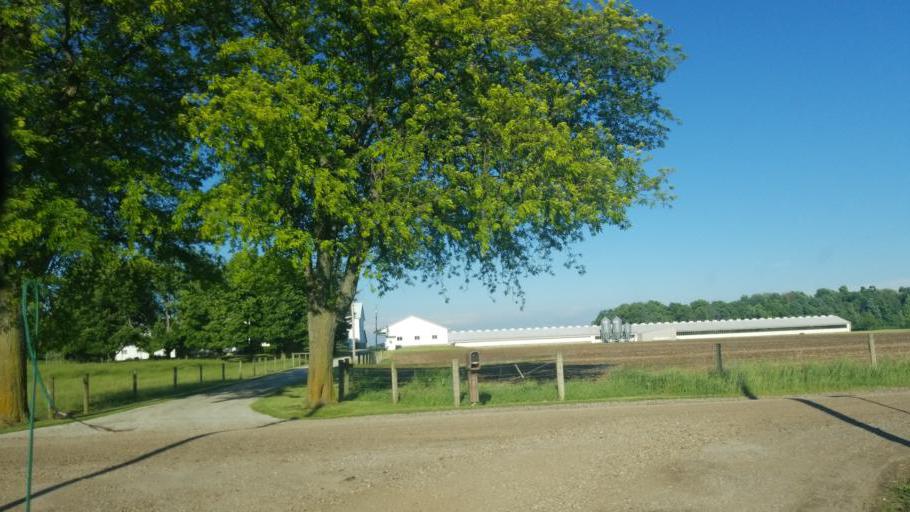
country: US
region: Indiana
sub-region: Marshall County
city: Bremen
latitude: 41.4098
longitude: -86.0977
